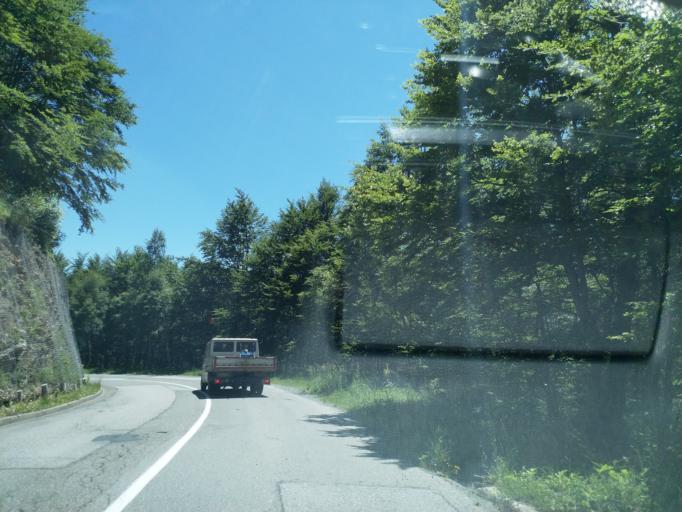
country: XK
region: Mitrovica
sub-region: Komuna e Leposaviqit
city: Leposaviq
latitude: 43.3125
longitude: 20.8604
